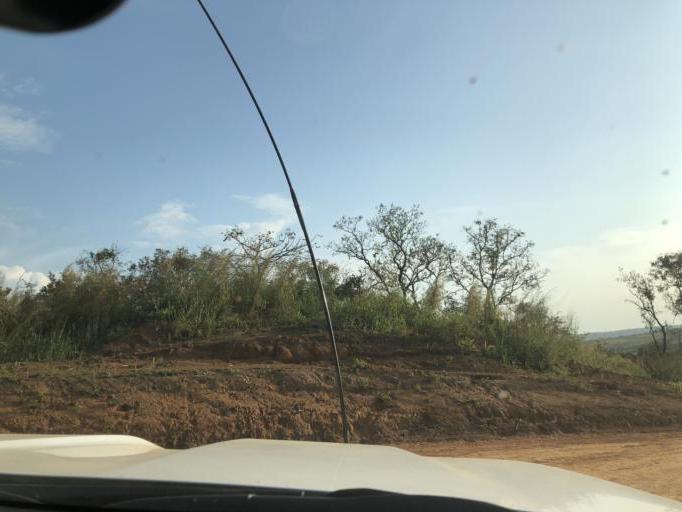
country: CF
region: Nana-Mambere
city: Bouar
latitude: 5.8950
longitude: 15.7622
